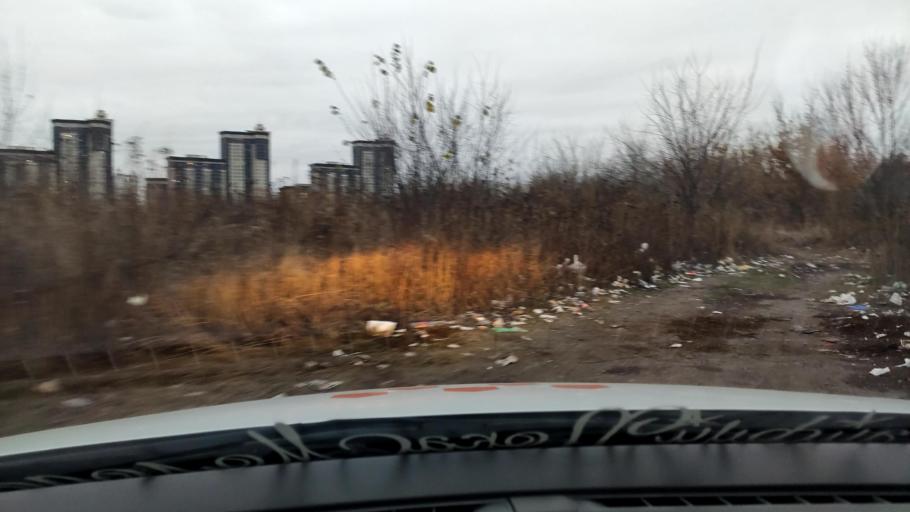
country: RU
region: Voronezj
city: Podgornoye
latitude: 51.7188
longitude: 39.1906
